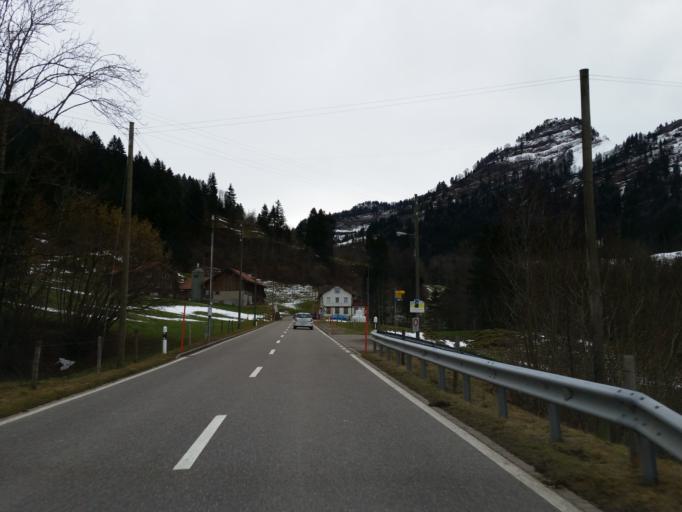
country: CH
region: Appenzell Ausserrhoden
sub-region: Bezirk Hinterland
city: Urnasch
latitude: 47.2873
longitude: 9.2795
